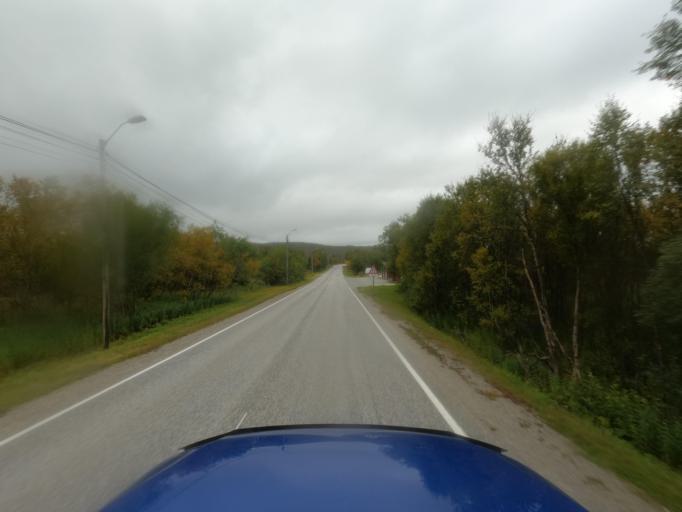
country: NO
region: Finnmark Fylke
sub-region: Porsanger
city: Lakselv
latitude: 70.4710
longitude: 25.0771
